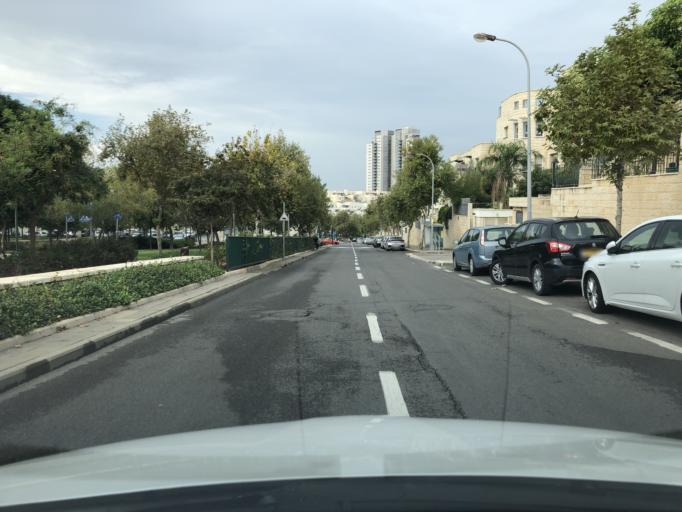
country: IL
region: Central District
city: Modiin
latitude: 31.9136
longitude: 35.0080
